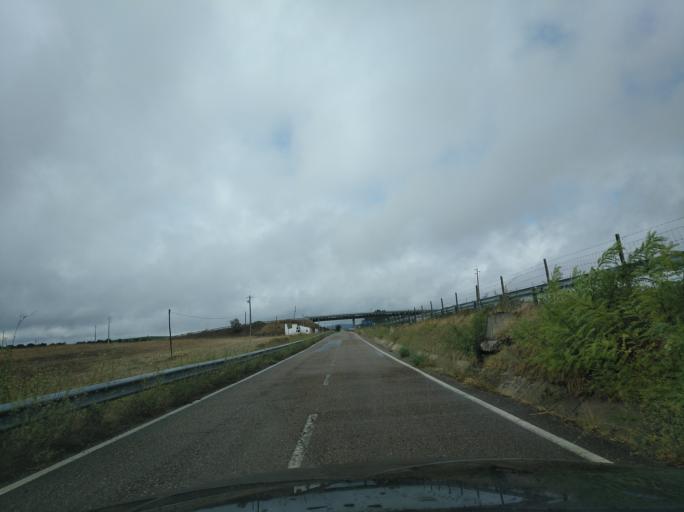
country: PT
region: Portalegre
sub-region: Elvas
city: Elvas
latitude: 38.8872
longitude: -7.0873
